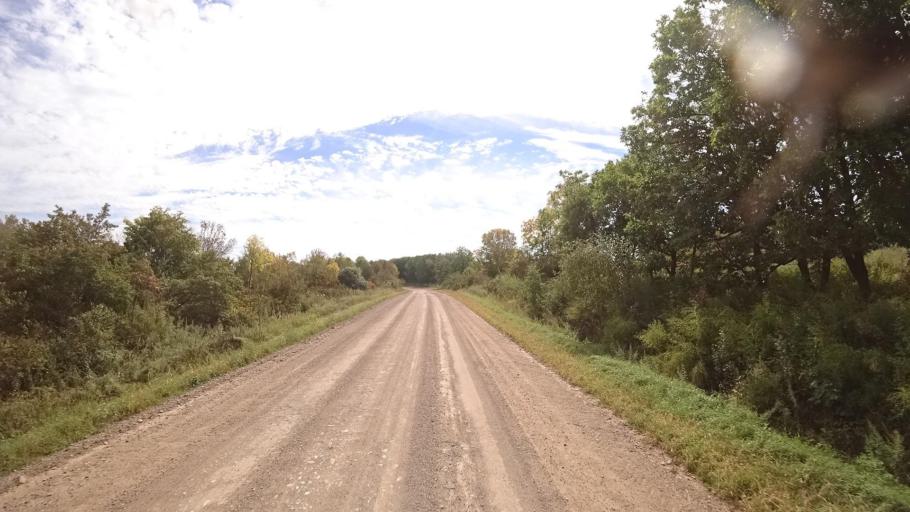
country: RU
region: Primorskiy
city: Yakovlevka
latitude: 44.5249
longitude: 133.5944
